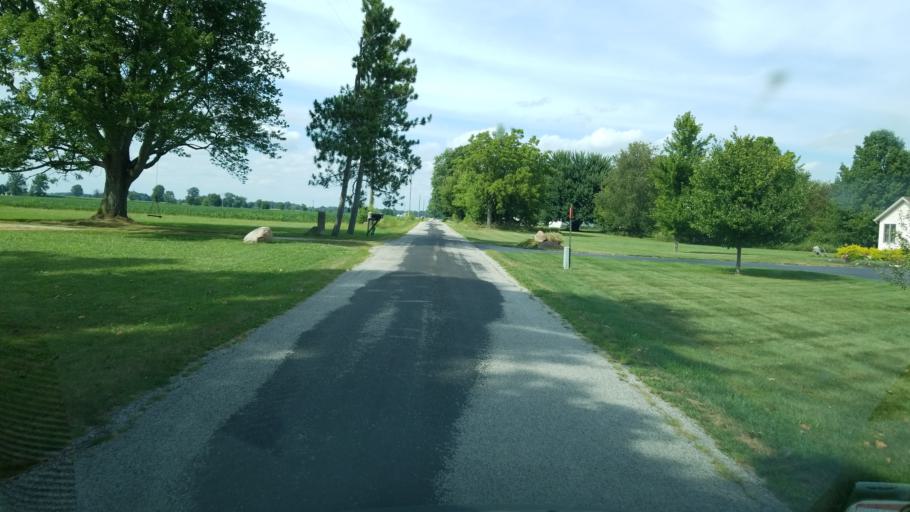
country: US
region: Ohio
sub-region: Marion County
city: Prospect
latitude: 40.4664
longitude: -83.1244
